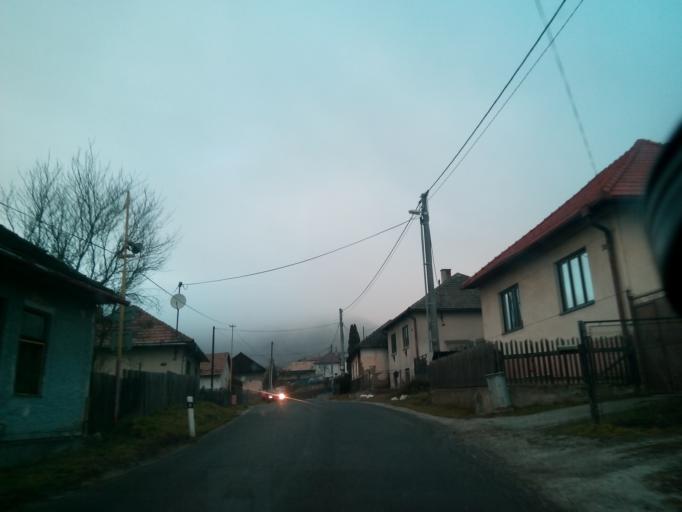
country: SK
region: Kosicky
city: Krompachy
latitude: 48.9323
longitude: 20.9401
